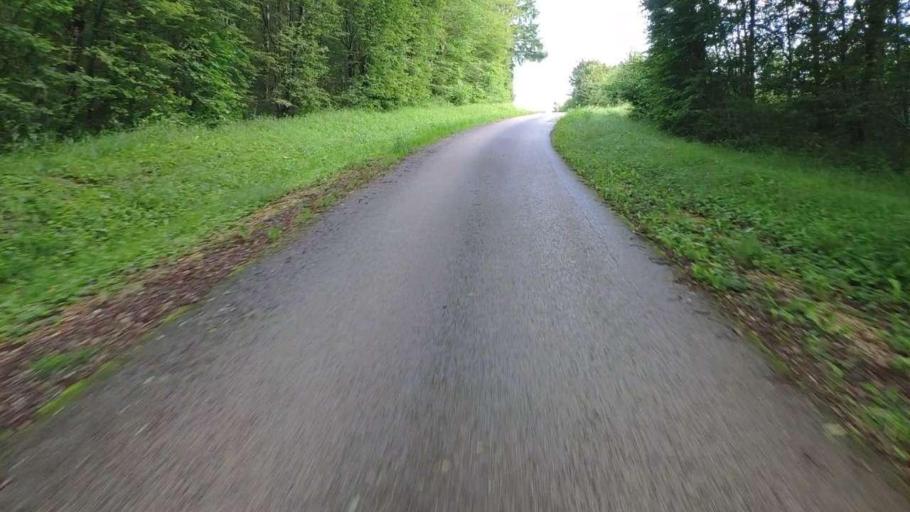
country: FR
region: Franche-Comte
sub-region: Departement du Jura
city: Poligny
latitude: 46.8001
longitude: 5.5962
